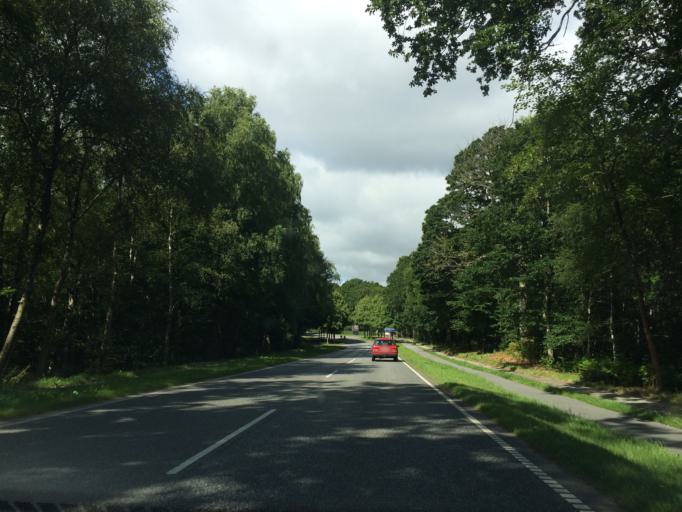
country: DK
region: Central Jutland
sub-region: Silkeborg Kommune
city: Silkeborg
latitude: 56.1694
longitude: 9.5797
